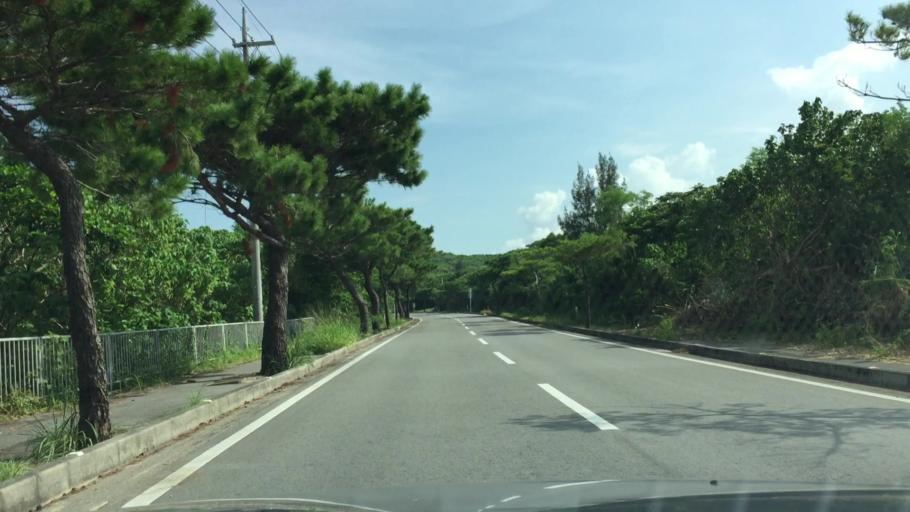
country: JP
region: Okinawa
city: Ishigaki
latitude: 24.4944
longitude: 124.2797
